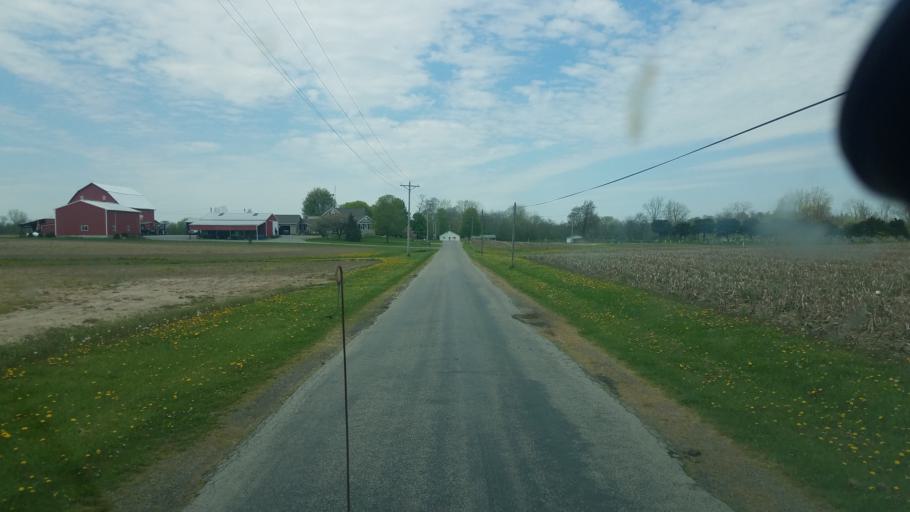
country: US
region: Ohio
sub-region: Hardin County
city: Ada
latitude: 40.7909
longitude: -83.8765
